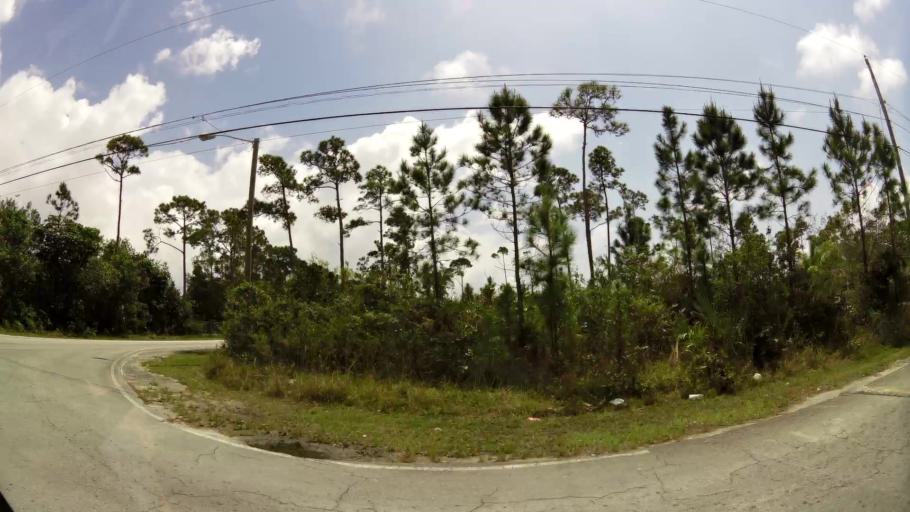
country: BS
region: Freeport
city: Lucaya
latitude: 26.5363
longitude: -78.6450
